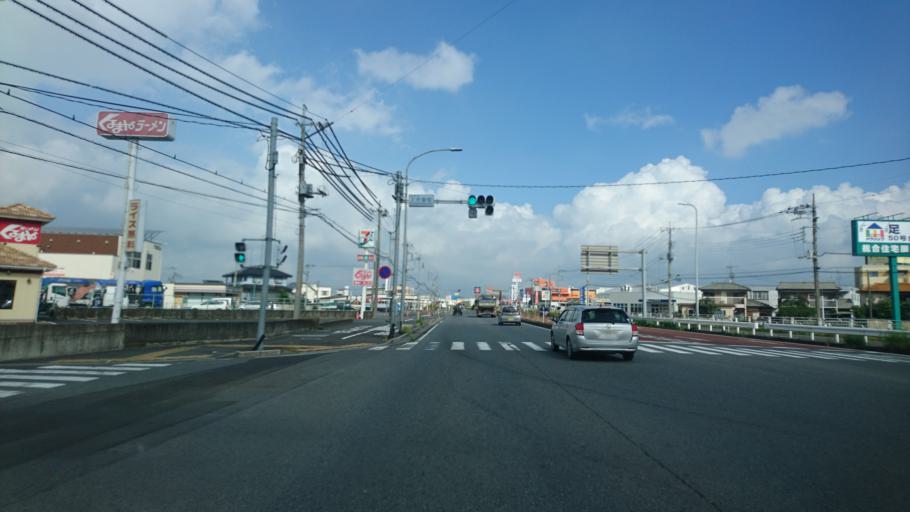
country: JP
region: Tochigi
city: Ashikaga
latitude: 36.3028
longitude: 139.4732
